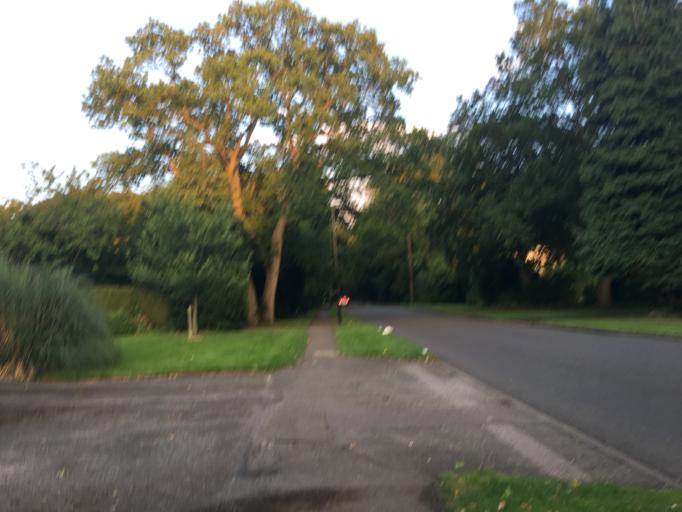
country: GB
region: England
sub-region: Coventry
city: Coventry
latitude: 52.3823
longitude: -1.5420
